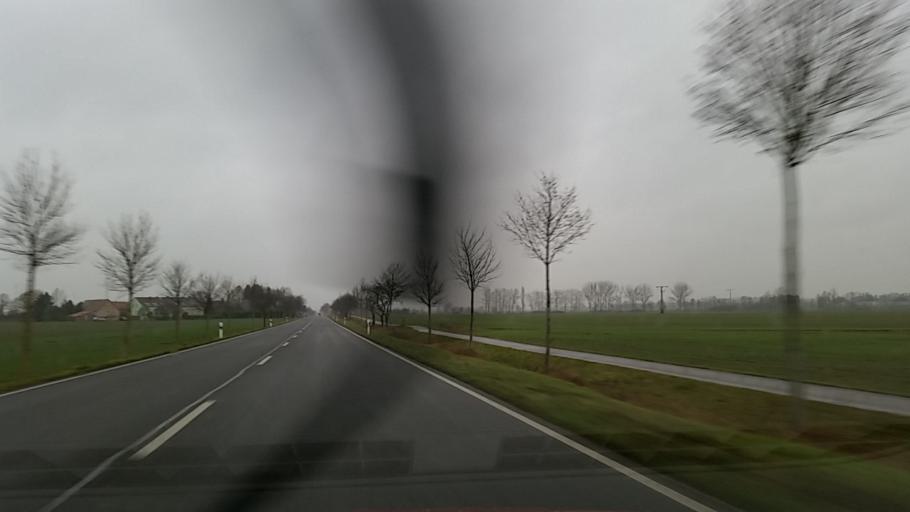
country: DE
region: Brandenburg
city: Dreetz
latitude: 52.8448
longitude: 12.5092
